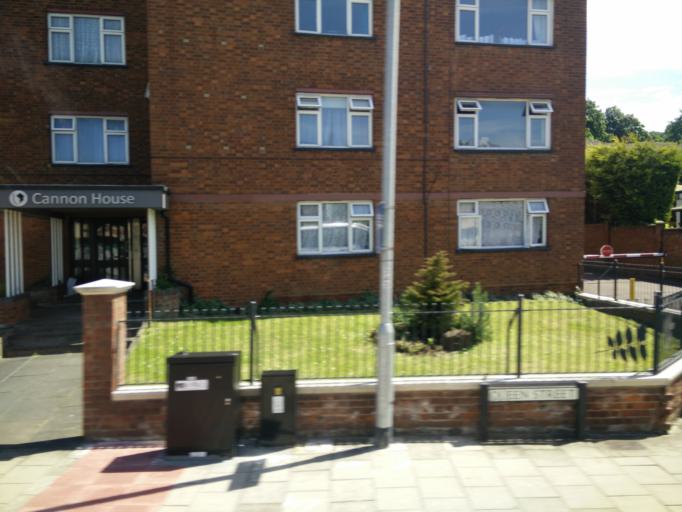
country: GB
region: England
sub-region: Hertfordshire
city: Hitchin
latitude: 51.9452
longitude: -0.2765
